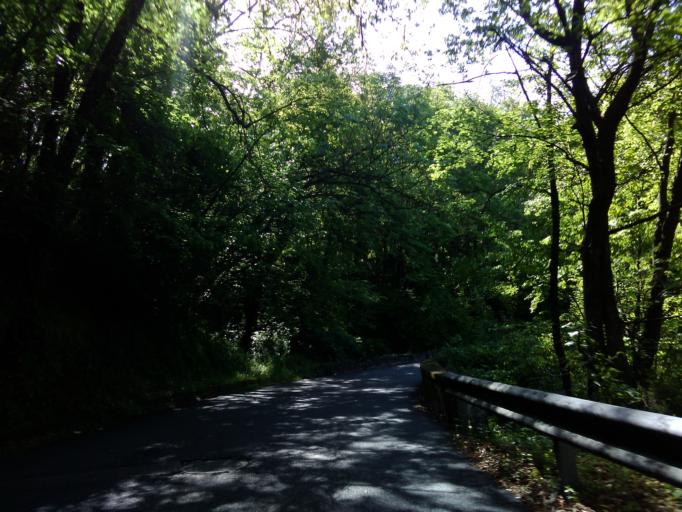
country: IT
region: Tuscany
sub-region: Provincia di Massa-Carrara
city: Carrara
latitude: 44.0795
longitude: 10.1086
